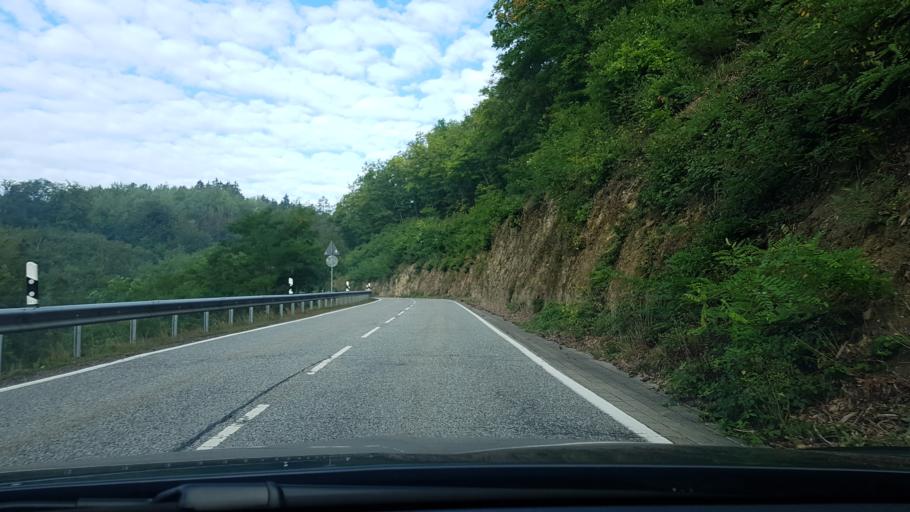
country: DE
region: Rheinland-Pfalz
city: Morshausen
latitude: 50.2098
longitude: 7.4388
